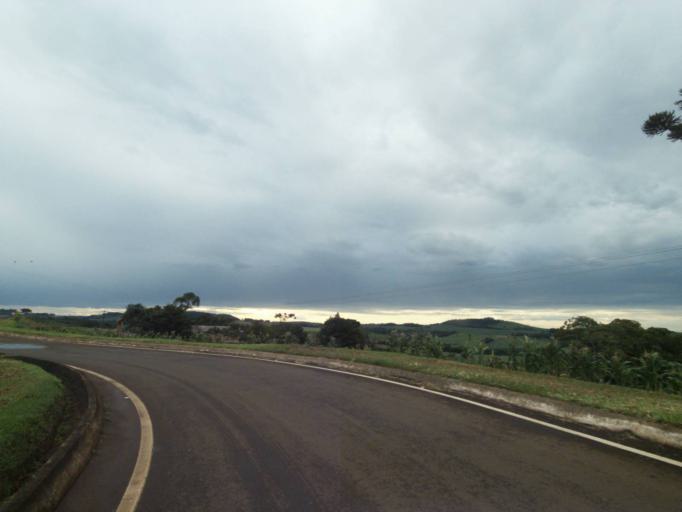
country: BR
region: Parana
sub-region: Guaraniacu
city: Guaraniacu
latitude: -25.0997
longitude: -52.8952
